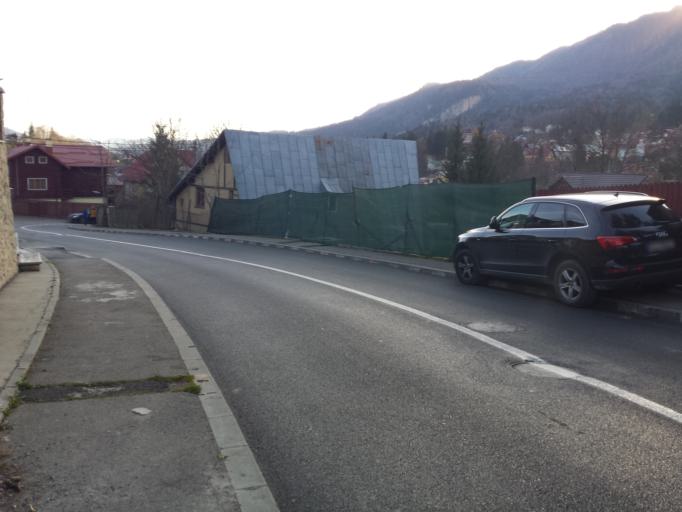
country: RO
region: Prahova
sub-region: Oras Busteni
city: Poiana Tapului
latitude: 45.3969
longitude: 25.5420
